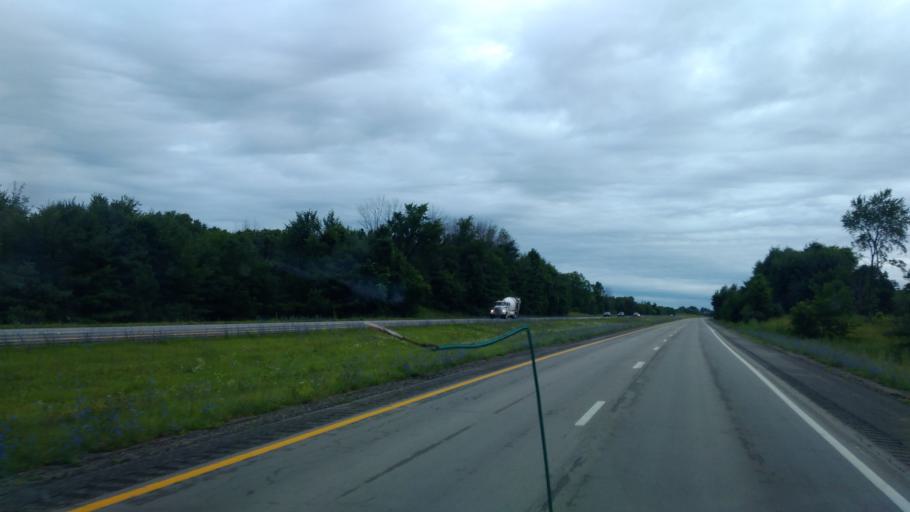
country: US
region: Ohio
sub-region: Columbiana County
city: Lisbon
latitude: 40.8169
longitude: -80.7453
